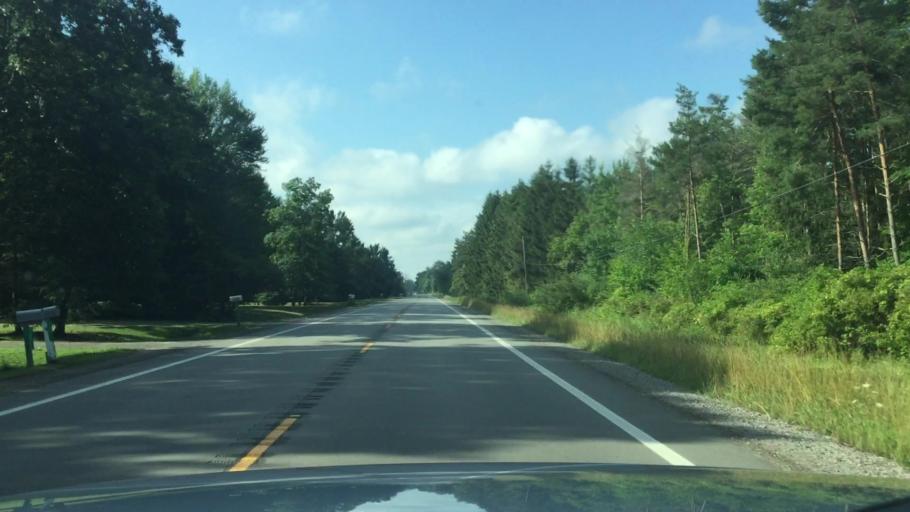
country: US
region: Michigan
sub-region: Genesee County
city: Clio
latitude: 43.2276
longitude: -83.7352
